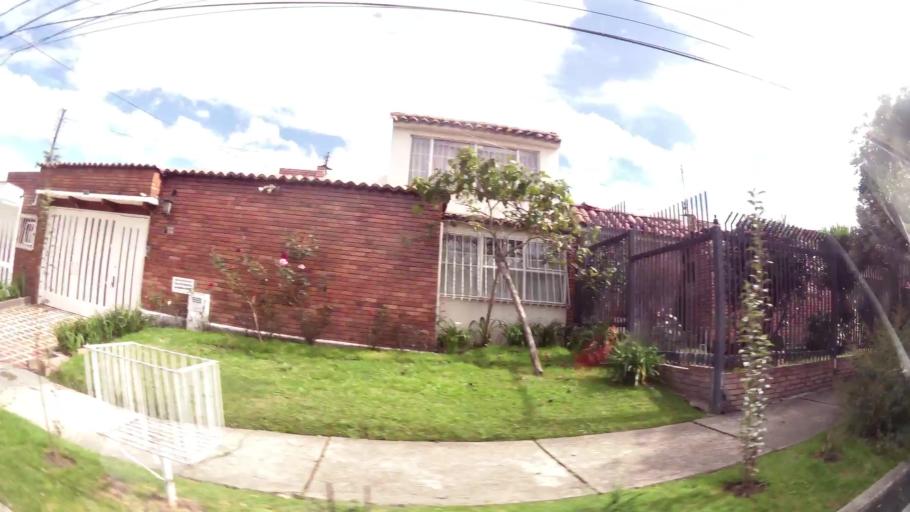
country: CO
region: Bogota D.C.
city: Barrio San Luis
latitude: 4.7083
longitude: -74.0778
